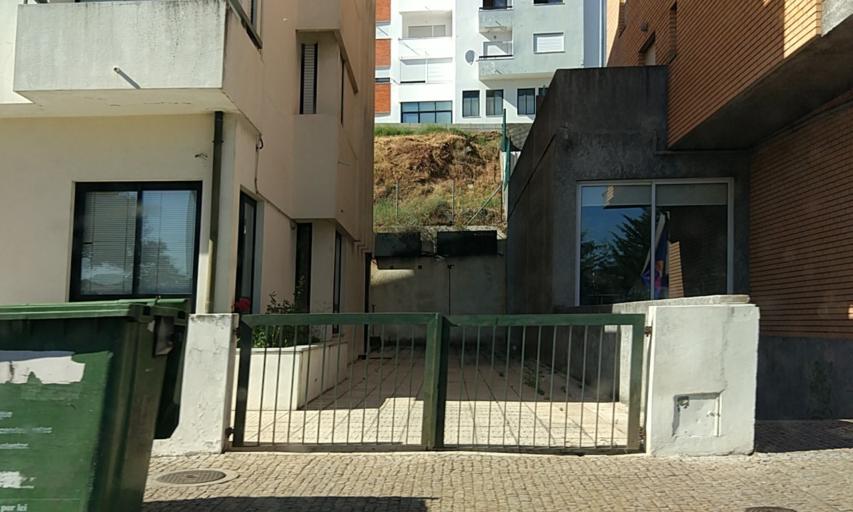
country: PT
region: Braganca
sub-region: Braganca Municipality
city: Braganca
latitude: 41.7997
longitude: -6.7670
